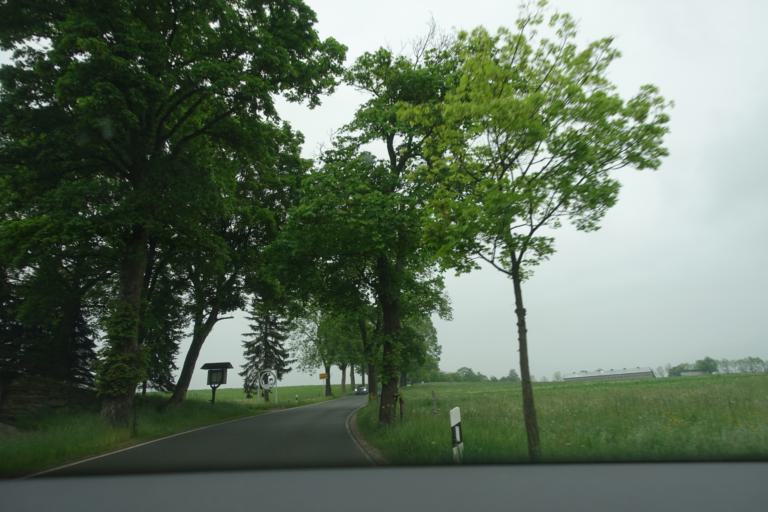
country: DE
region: Saxony
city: Eppendorf
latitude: 50.7878
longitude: 13.2719
